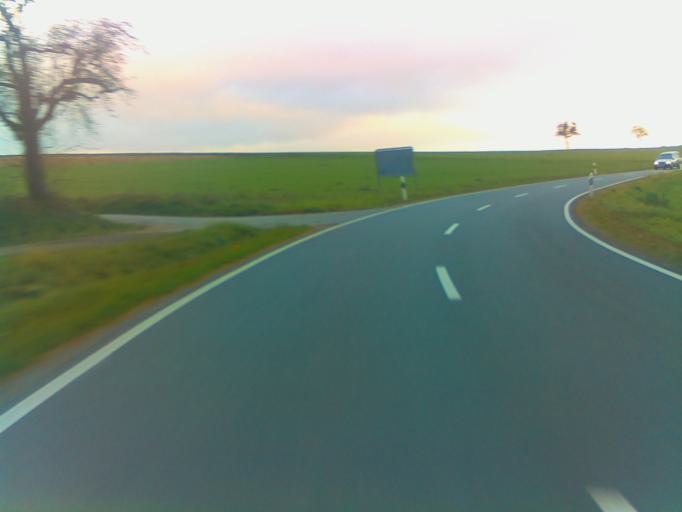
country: DE
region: Hesse
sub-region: Regierungsbezirk Darmstadt
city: Beerfelden
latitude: 49.5743
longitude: 8.9588
